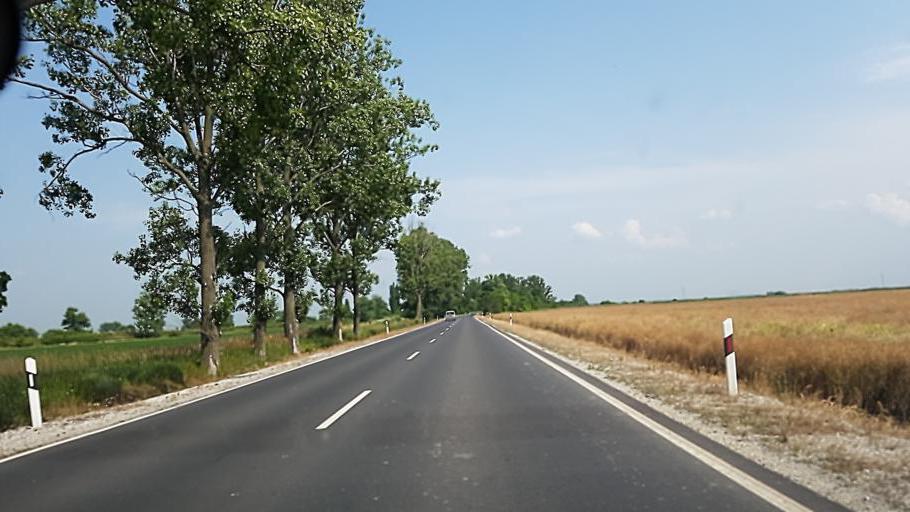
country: HU
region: Heves
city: Tiszanana
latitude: 47.6706
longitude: 20.5537
